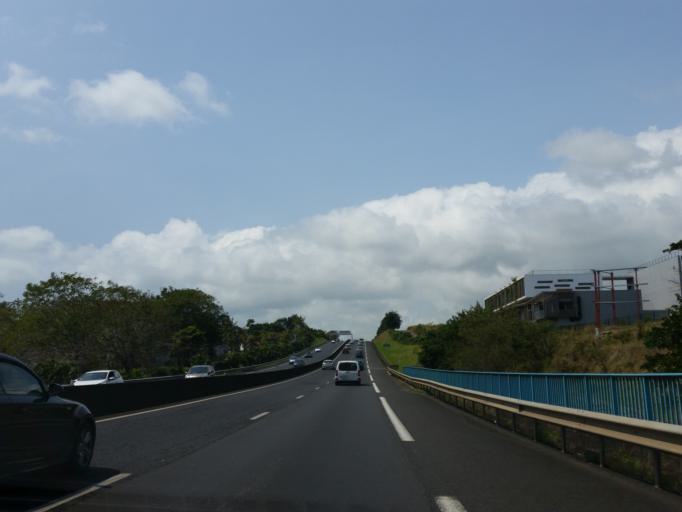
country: RE
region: Reunion
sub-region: Reunion
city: Sainte-Marie
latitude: -20.9000
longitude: 55.5256
